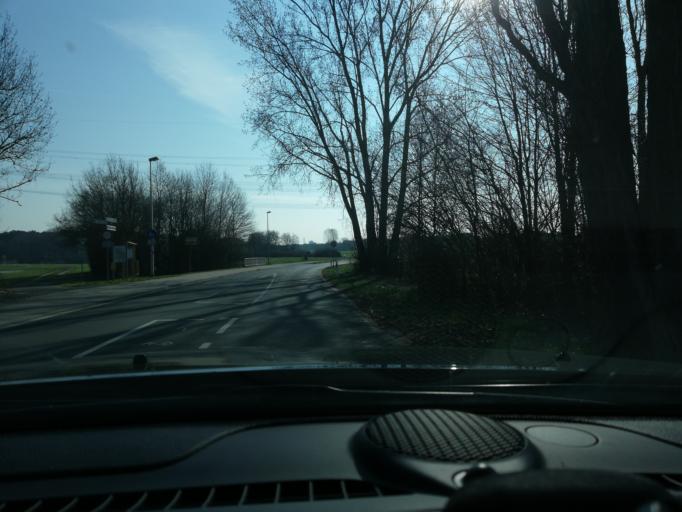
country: DE
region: Bavaria
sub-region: Regierungsbezirk Mittelfranken
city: Hessdorf
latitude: 49.6001
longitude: 10.9418
